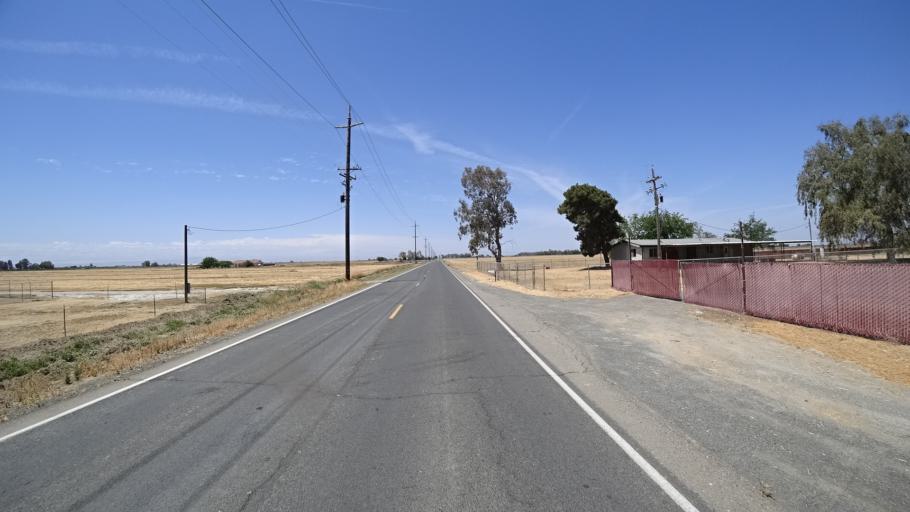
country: US
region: California
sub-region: Kings County
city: Lemoore
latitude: 36.2402
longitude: -119.7847
